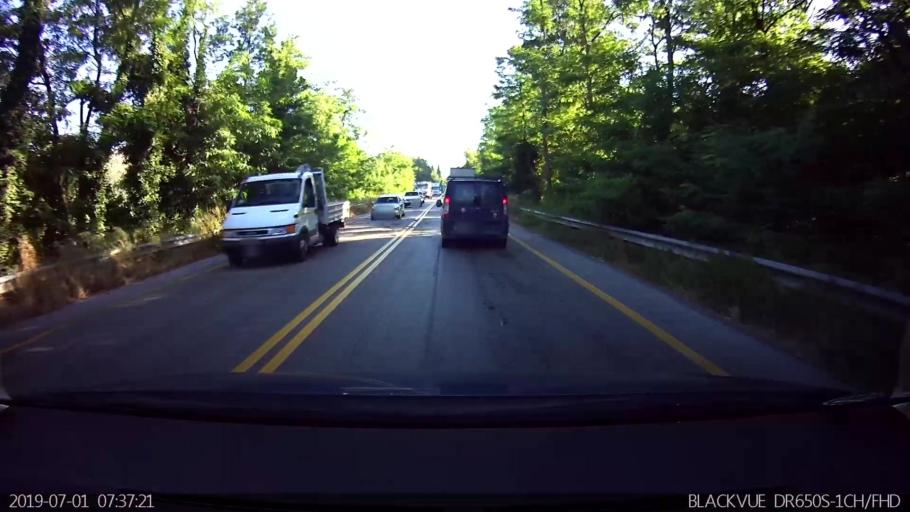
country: IT
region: Latium
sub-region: Provincia di Frosinone
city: Giuliano di Roma
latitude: 41.5374
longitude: 13.2669
